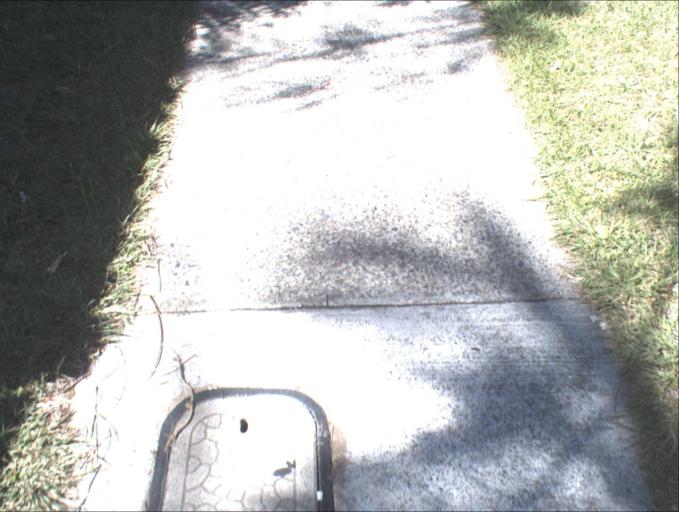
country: AU
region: Queensland
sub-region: Logan
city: Rochedale South
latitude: -27.6042
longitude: 153.1103
